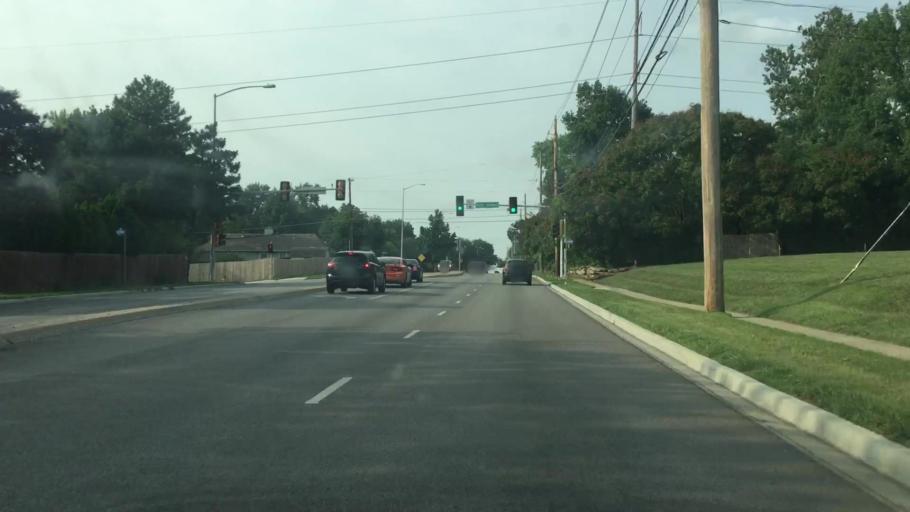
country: US
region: Kansas
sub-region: Johnson County
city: Overland Park
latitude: 38.9635
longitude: -94.6863
